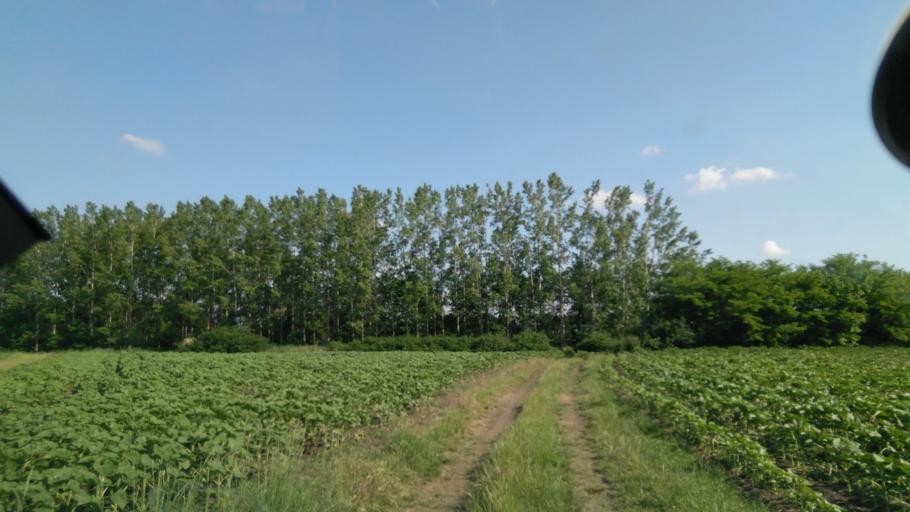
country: HU
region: Bekes
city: Doboz
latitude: 46.7012
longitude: 21.2376
